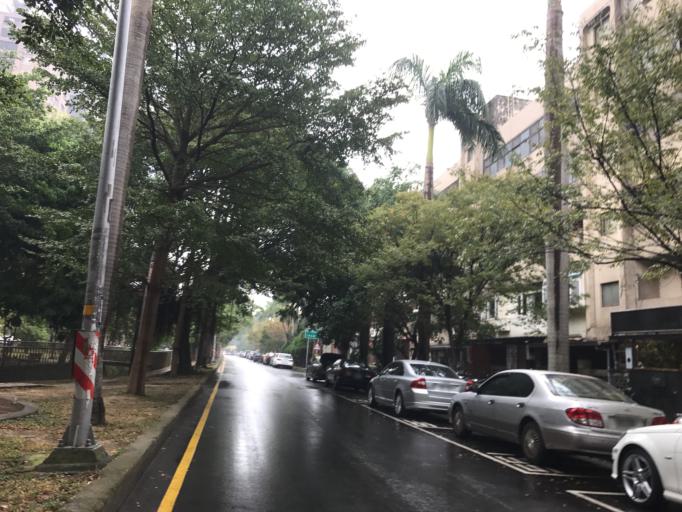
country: TW
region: Taiwan
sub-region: Hsinchu
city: Hsinchu
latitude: 24.8084
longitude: 120.9756
